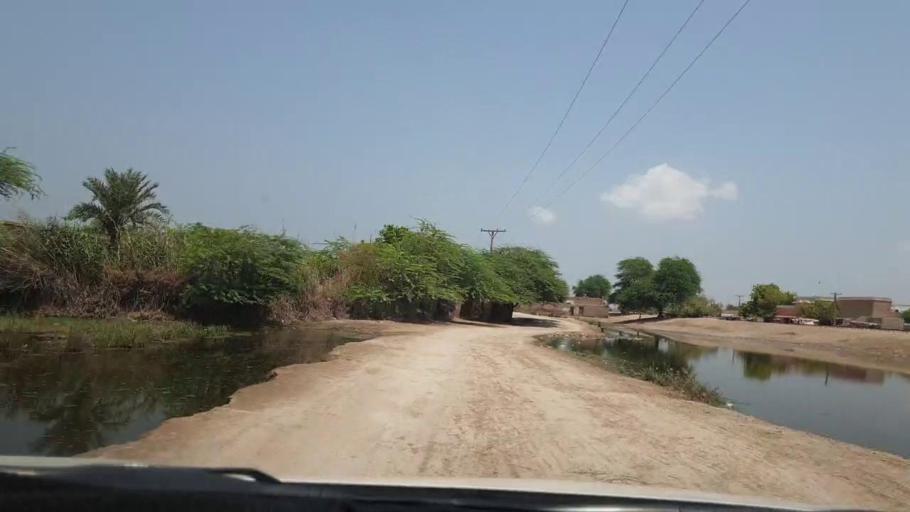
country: PK
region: Sindh
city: Radhan
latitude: 27.2445
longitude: 67.9867
